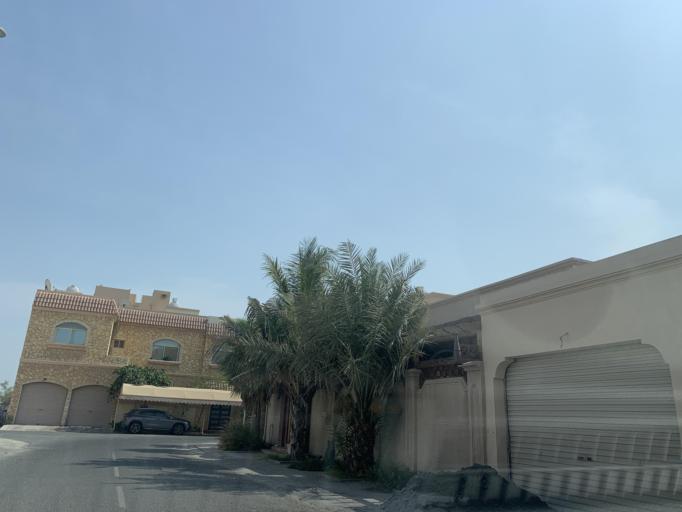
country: BH
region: Muharraq
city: Al Hadd
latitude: 26.2642
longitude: 50.6565
